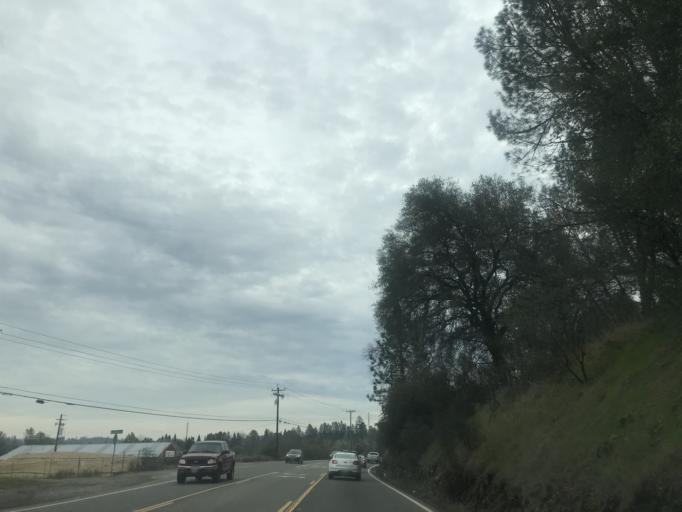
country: US
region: California
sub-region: El Dorado County
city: Diamond Springs
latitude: 38.7026
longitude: -120.8247
